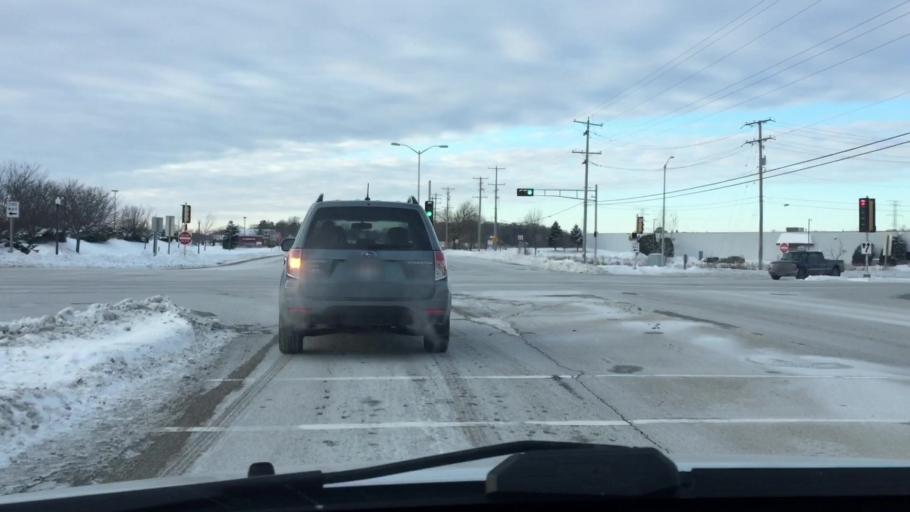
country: US
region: Wisconsin
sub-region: Waukesha County
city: Sussex
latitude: 43.1371
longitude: -88.2435
